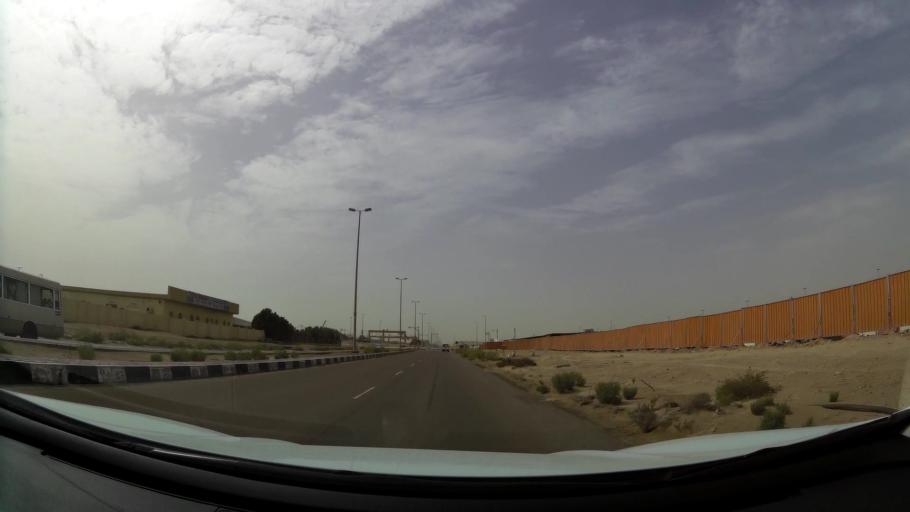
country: AE
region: Abu Dhabi
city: Abu Dhabi
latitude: 24.3357
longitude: 54.5055
